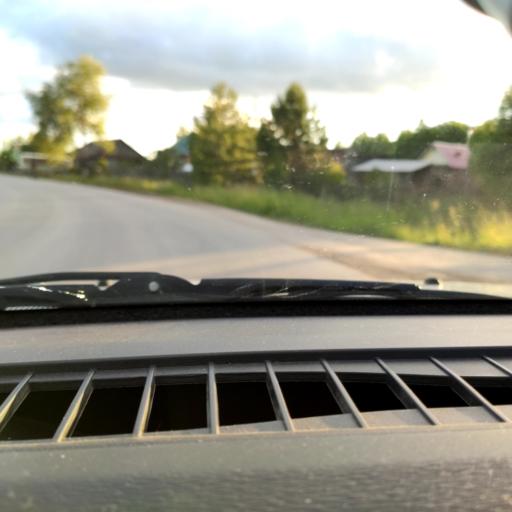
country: RU
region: Perm
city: Polazna
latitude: 58.2118
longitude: 56.5099
